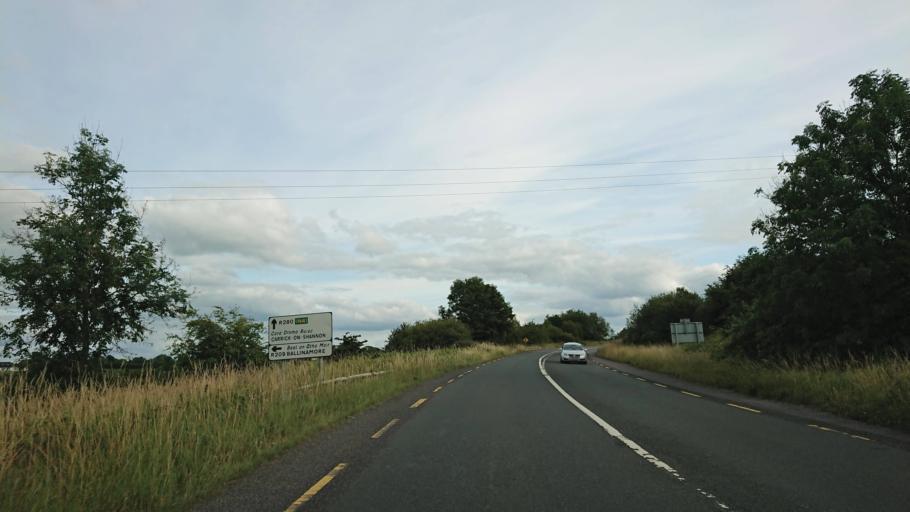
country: IE
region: Connaught
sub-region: County Leitrim
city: Carrick-on-Shannon
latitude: 53.9784
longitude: -8.0614
